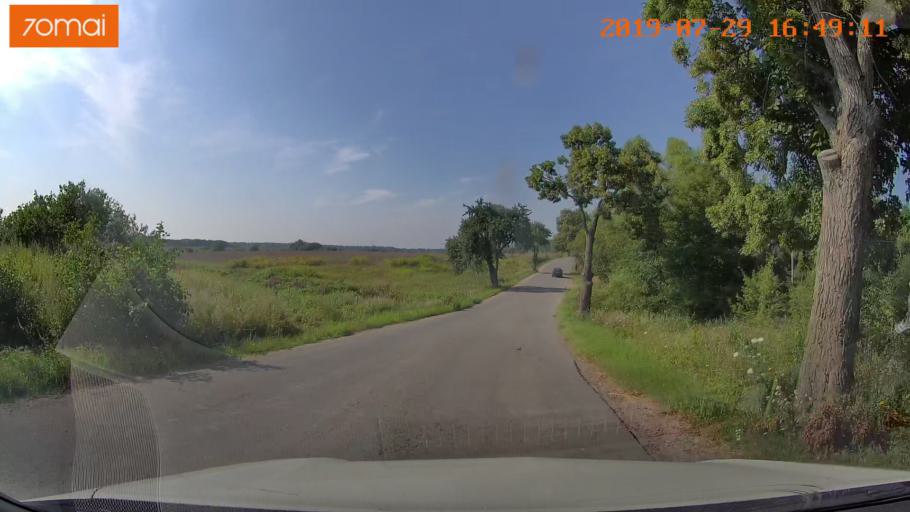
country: RU
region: Kaliningrad
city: Primorsk
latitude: 54.7918
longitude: 20.0675
